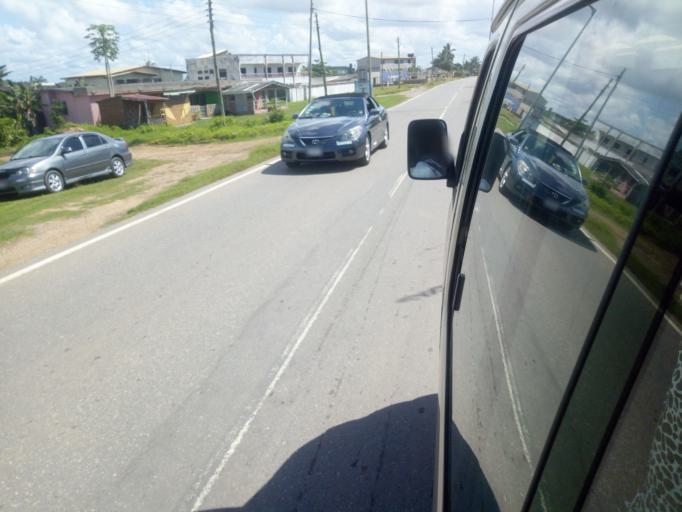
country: GH
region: Central
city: Elmina
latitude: 5.0941
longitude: -1.3374
